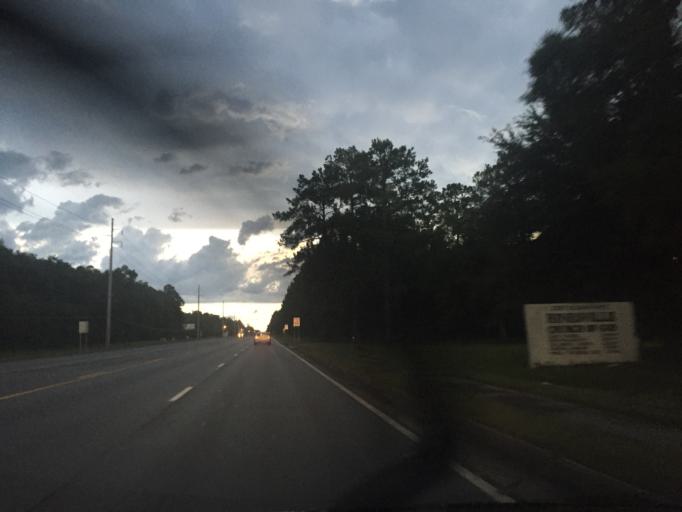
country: US
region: Georgia
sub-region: Liberty County
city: Hinesville
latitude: 31.8551
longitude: -81.5584
